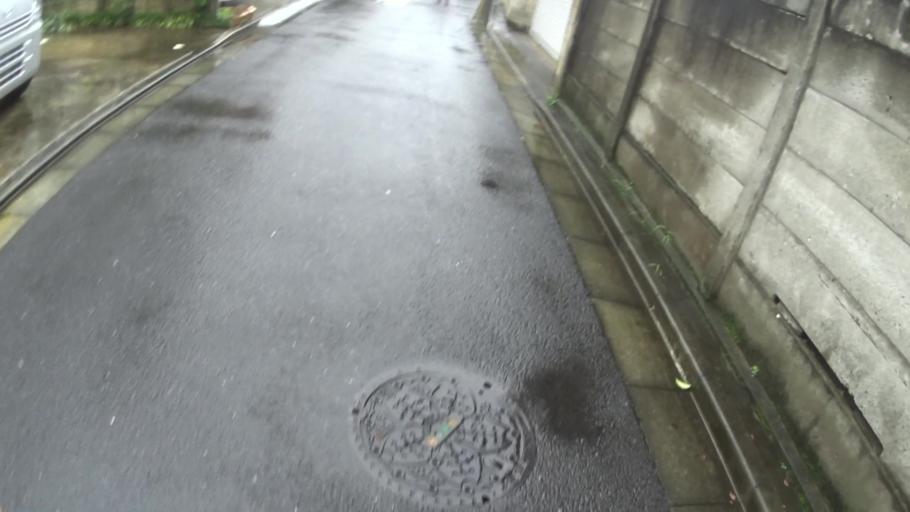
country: JP
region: Saitama
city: Wako
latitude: 35.7449
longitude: 139.6651
